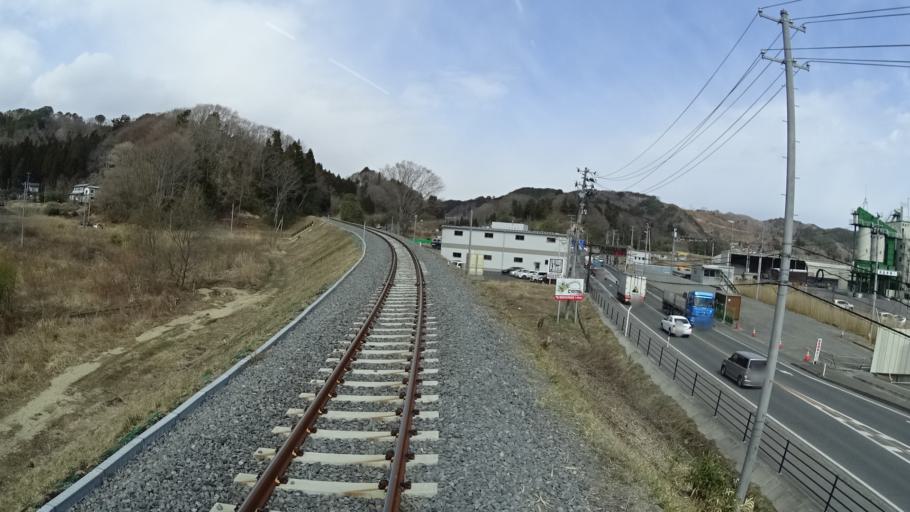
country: JP
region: Iwate
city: Miyako
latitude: 39.5906
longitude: 141.9454
